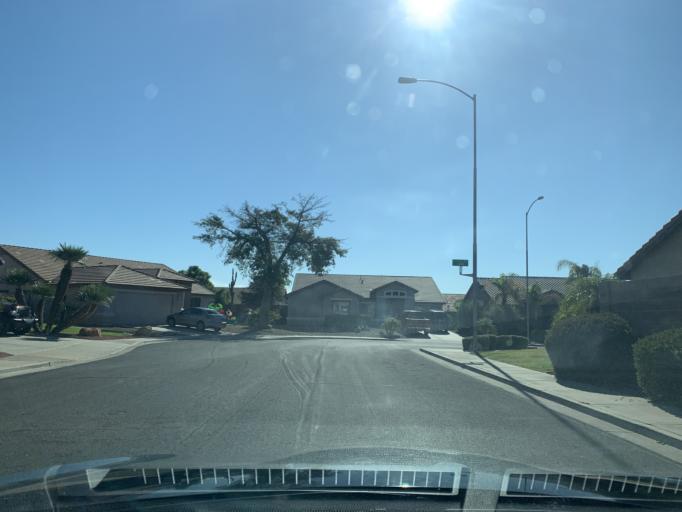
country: US
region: Arizona
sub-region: Pinal County
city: Apache Junction
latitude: 33.3830
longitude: -111.6203
